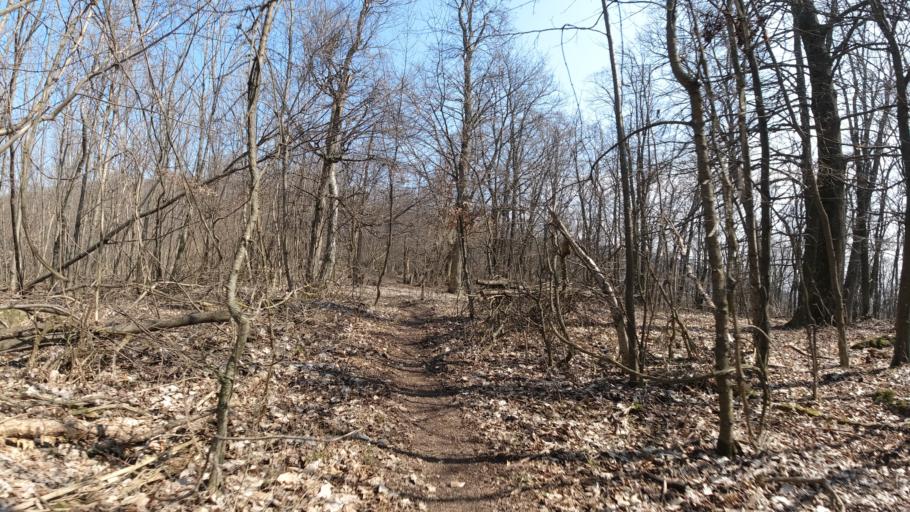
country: SK
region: Trnavsky
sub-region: Okres Trnava
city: Piestany
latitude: 48.5828
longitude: 17.9280
